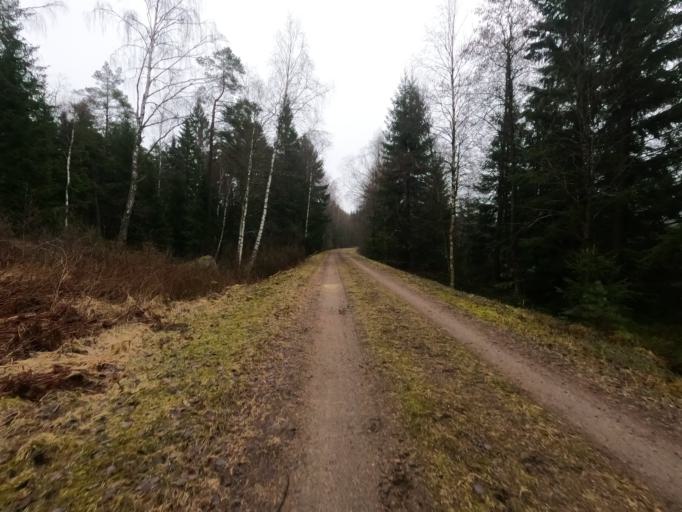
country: SE
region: Halland
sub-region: Hylte Kommun
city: Hyltebruk
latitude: 56.8034
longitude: 13.2339
